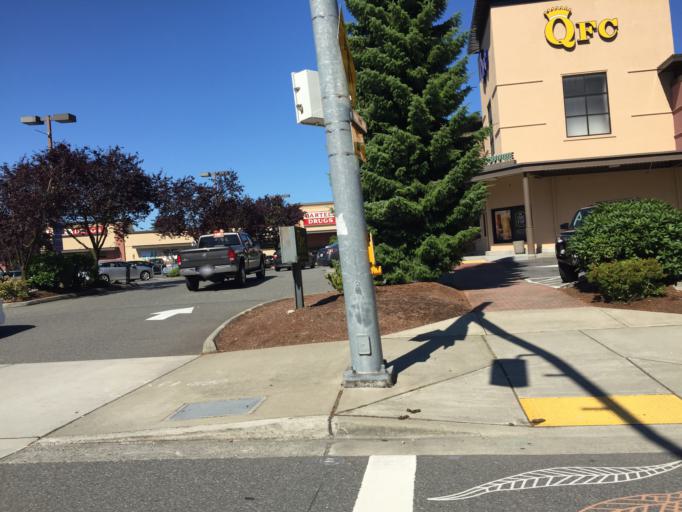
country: US
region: Washington
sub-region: King County
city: Bellevue
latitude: 47.6183
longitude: -122.2044
